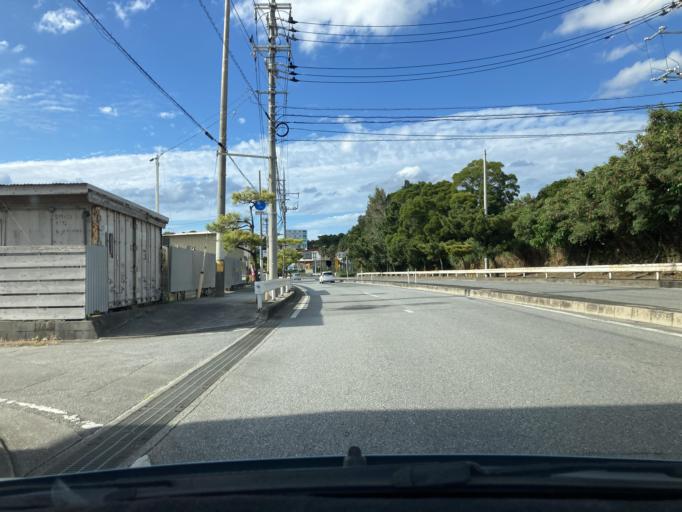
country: JP
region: Okinawa
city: Ishikawa
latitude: 26.4337
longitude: 127.8307
